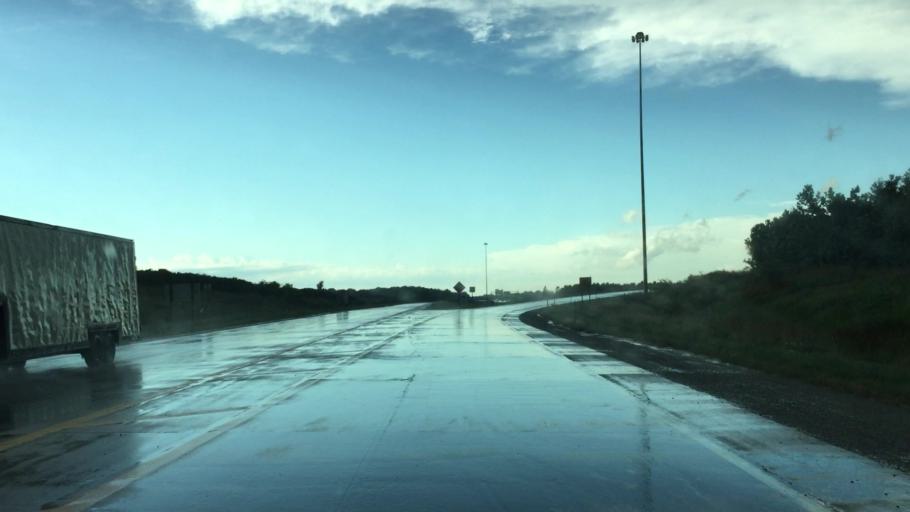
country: US
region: Iowa
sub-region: Henry County
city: Mount Pleasant
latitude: 40.9914
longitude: -91.5445
